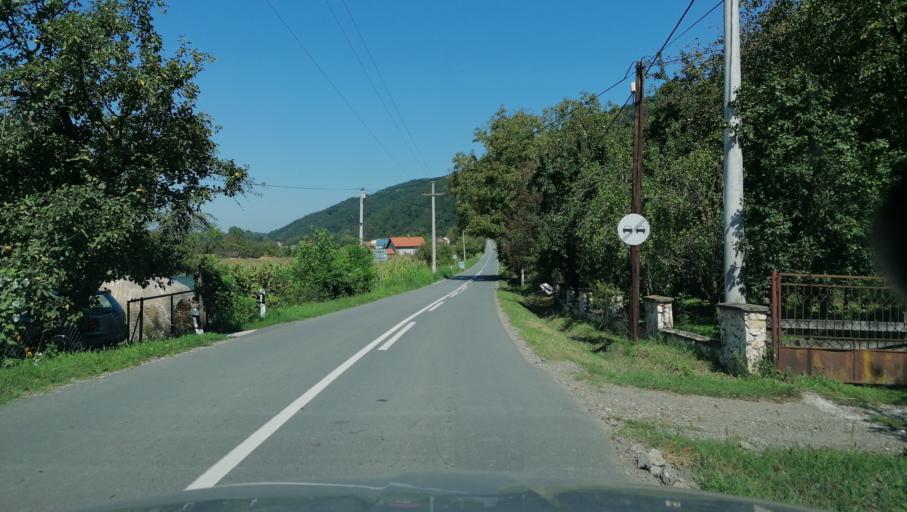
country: RS
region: Central Serbia
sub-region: Raski Okrug
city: Vrnjacka Banja
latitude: 43.6551
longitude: 20.9346
